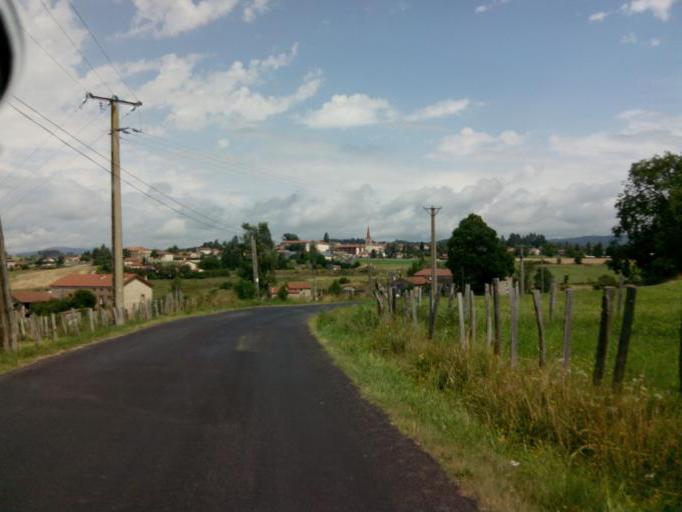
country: FR
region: Rhone-Alpes
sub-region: Departement de la Loire
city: Usson-en-Forez
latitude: 45.3811
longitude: 3.9439
